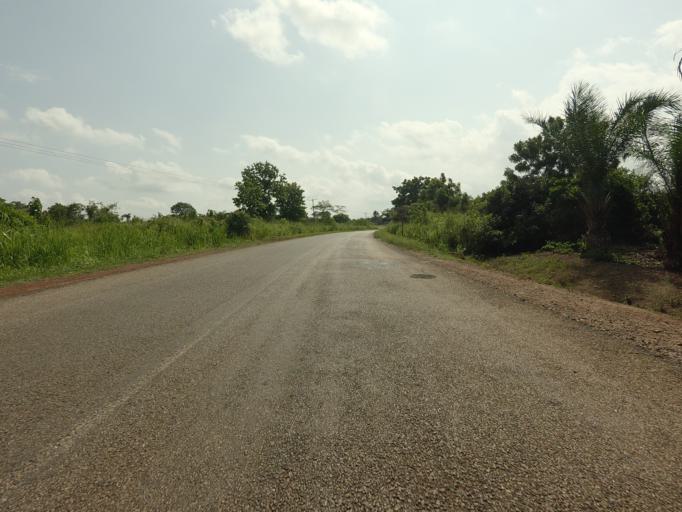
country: GH
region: Volta
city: Ho
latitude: 6.3937
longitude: 0.8003
